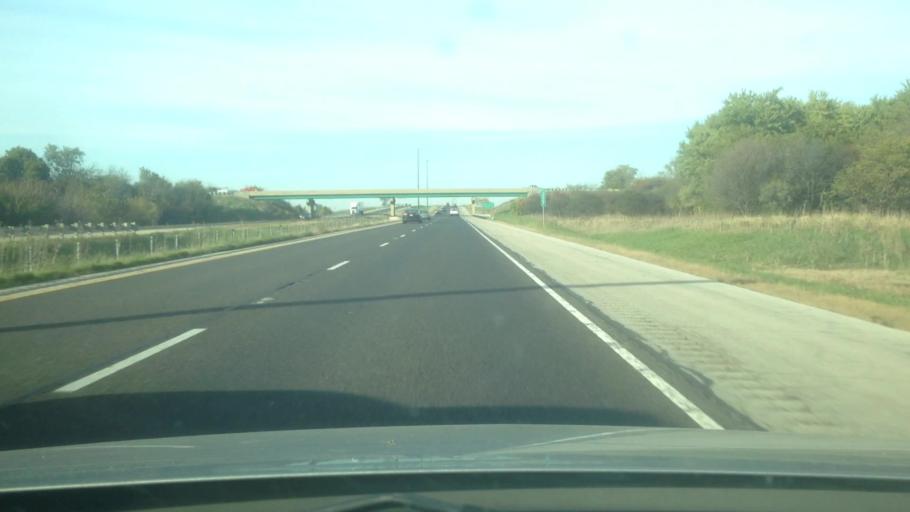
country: US
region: Illinois
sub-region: Will County
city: Peotone
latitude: 41.3222
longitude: -87.8200
